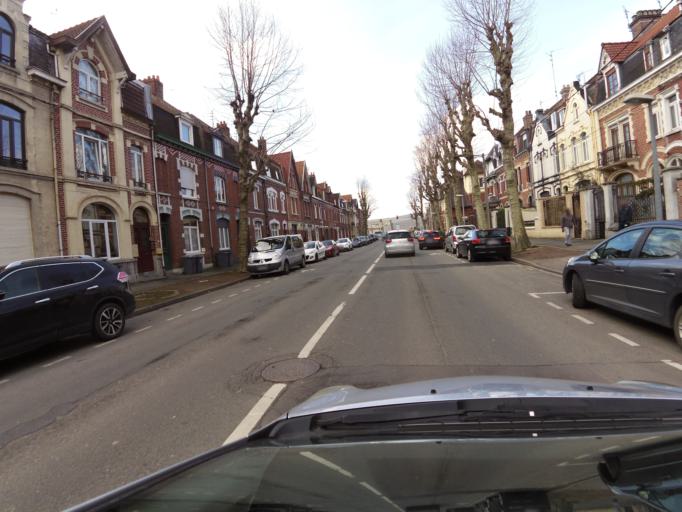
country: FR
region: Nord-Pas-de-Calais
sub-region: Departement du Nord
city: Armentieres
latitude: 50.6850
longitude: 2.8694
